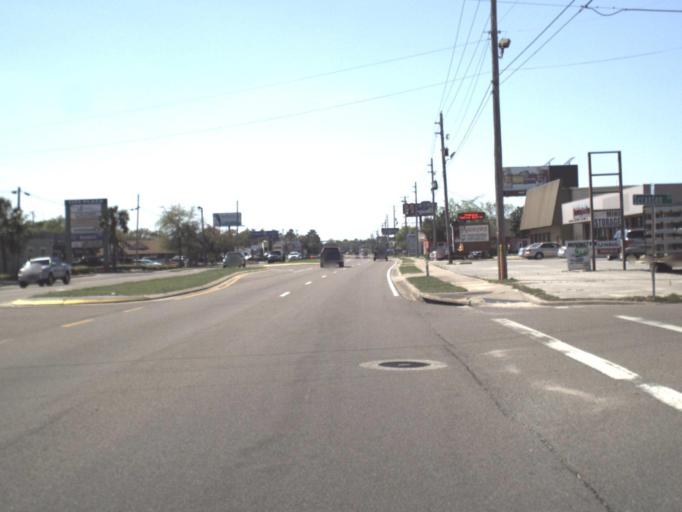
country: US
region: Florida
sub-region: Okaloosa County
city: Ocean City
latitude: 30.4427
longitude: -86.6005
